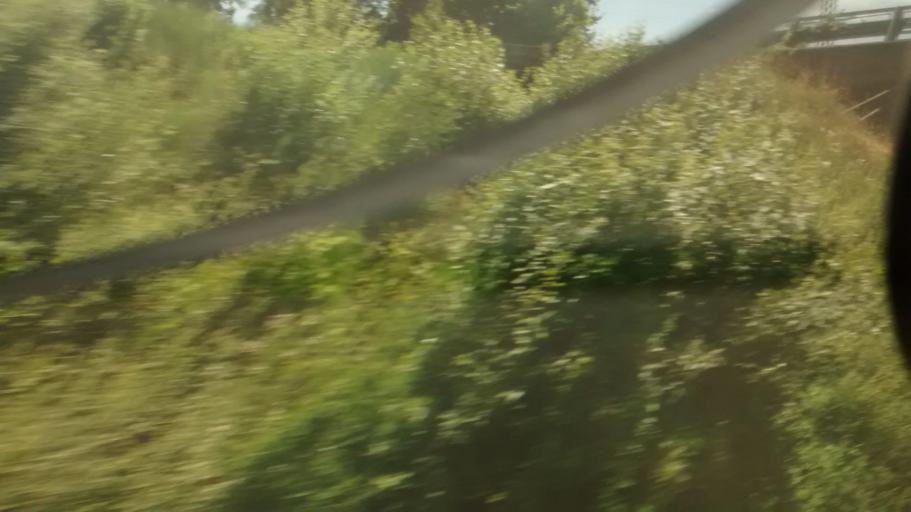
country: FR
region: Rhone-Alpes
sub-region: Departement de l'Ain
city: Beynost
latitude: 45.8549
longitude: 4.9963
